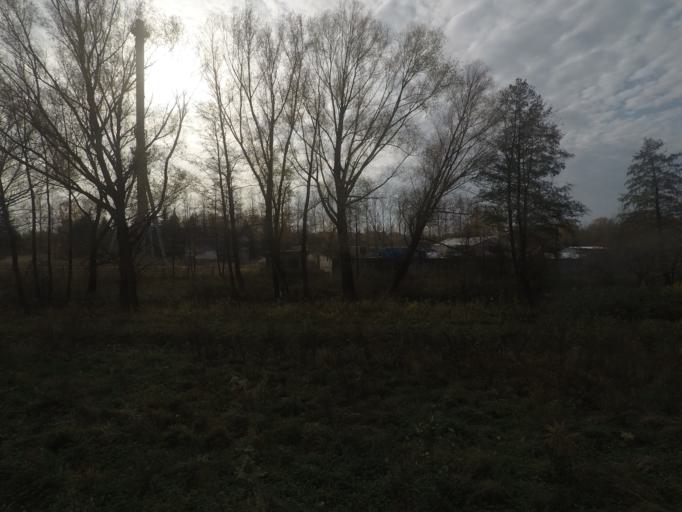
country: PL
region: Subcarpathian Voivodeship
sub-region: Powiat ropczycko-sedziszowski
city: Sedziszow Malopolski
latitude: 50.0732
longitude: 21.7122
